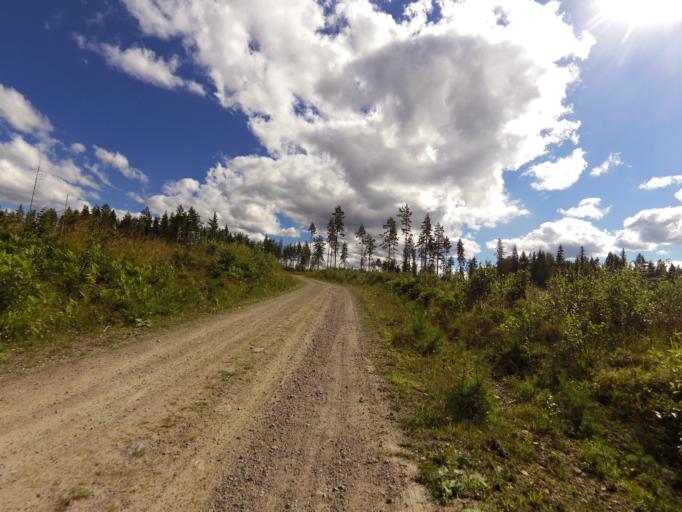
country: SE
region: Gaevleborg
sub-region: Hofors Kommun
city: Hofors
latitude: 60.5258
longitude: 16.2337
